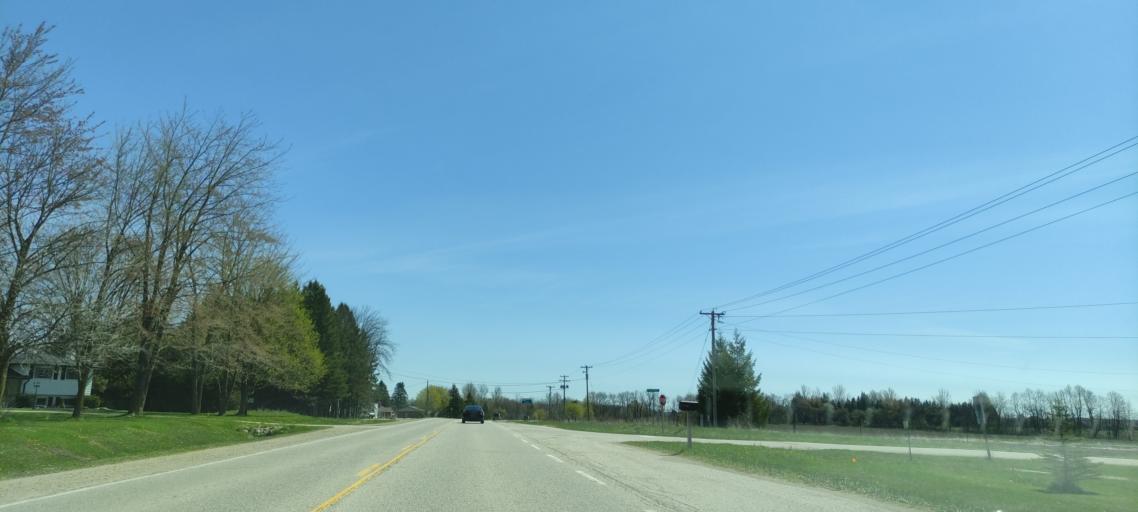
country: CA
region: Ontario
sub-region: Wellington County
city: Guelph
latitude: 43.5756
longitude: -80.3752
